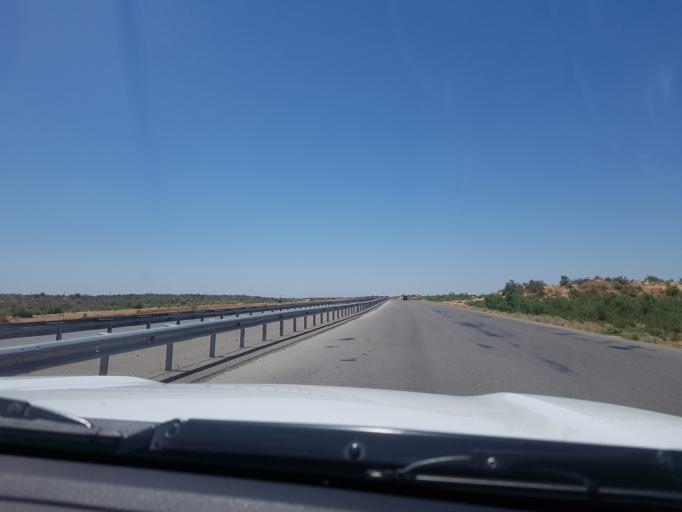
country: TM
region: Mary
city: Mary
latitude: 37.3669
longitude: 61.4474
